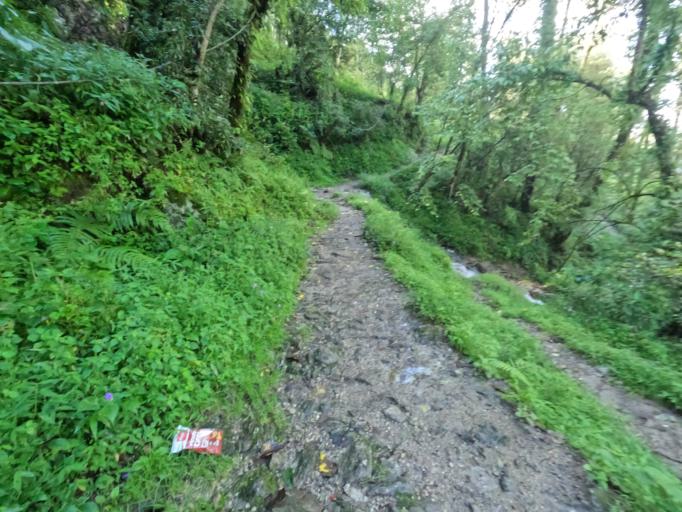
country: NP
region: Eastern Region
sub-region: Sagarmatha Zone
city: Namche Bazar
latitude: 27.4923
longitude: 86.5827
